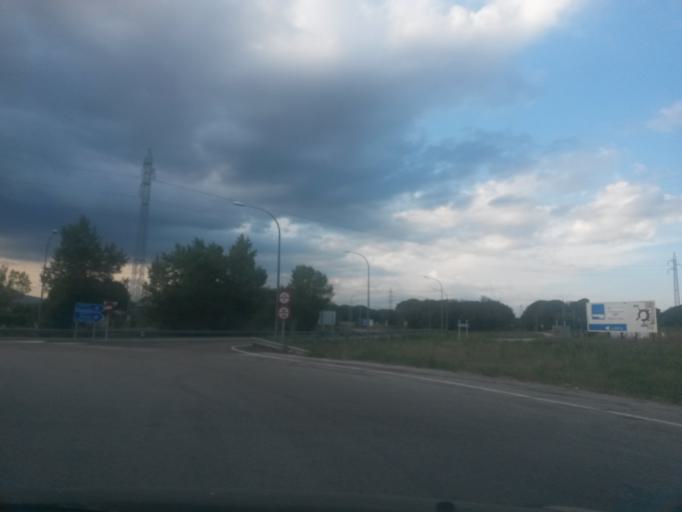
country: ES
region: Catalonia
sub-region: Provincia de Girona
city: Riudellots de la Selva
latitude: 41.8932
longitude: 2.7798
